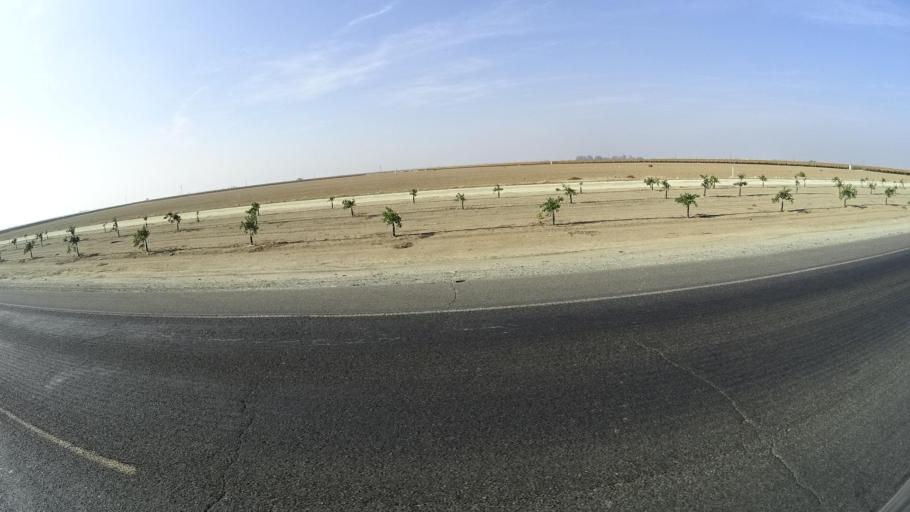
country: US
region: California
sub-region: Tulare County
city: Richgrove
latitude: 35.7266
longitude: -119.1543
